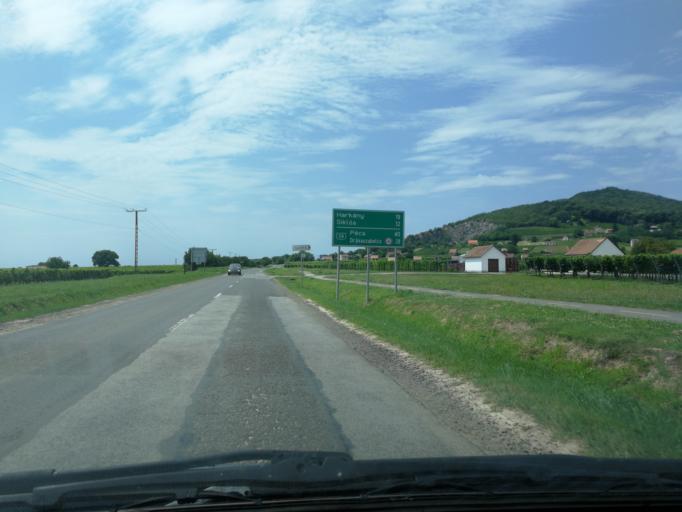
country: HU
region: Baranya
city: Villany
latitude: 45.8593
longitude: 18.4392
